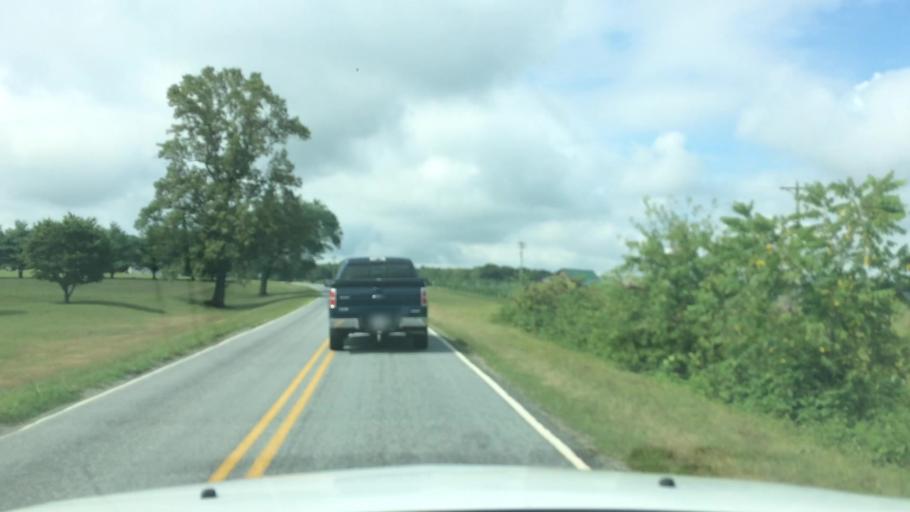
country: US
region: North Carolina
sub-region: Yadkin County
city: Jonesville
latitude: 36.1030
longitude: -80.8608
